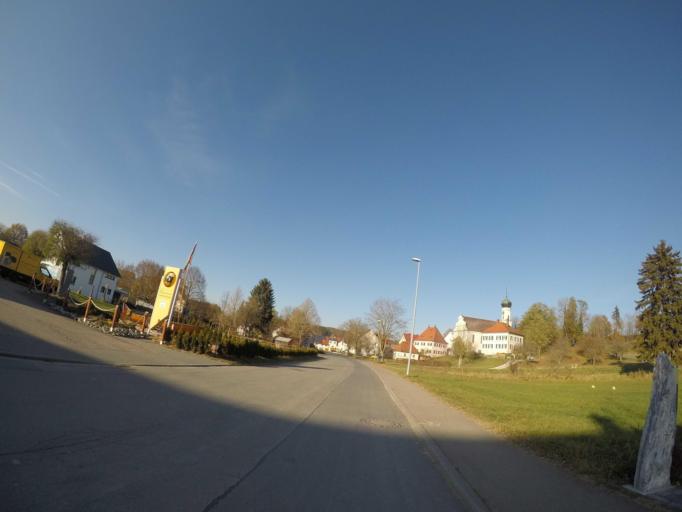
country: DE
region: Baden-Wuerttemberg
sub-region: Tuebingen Region
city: Grundsheim
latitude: 48.1768
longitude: 9.6678
